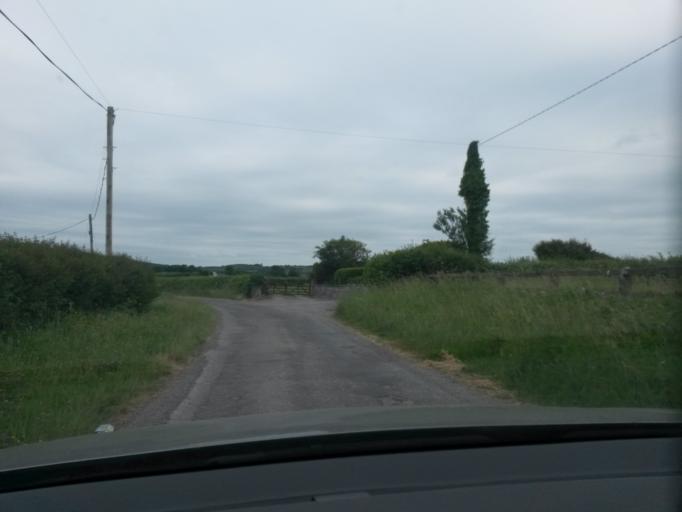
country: IE
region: Munster
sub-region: An Clar
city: Ennis
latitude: 52.9139
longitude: -9.0532
